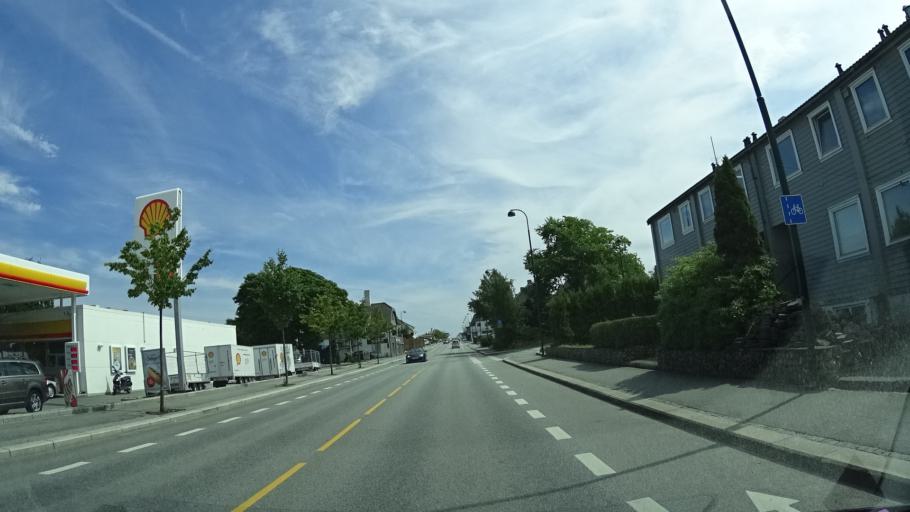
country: NO
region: Rogaland
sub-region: Stavanger
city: Stavanger
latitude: 58.9781
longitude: 5.7010
